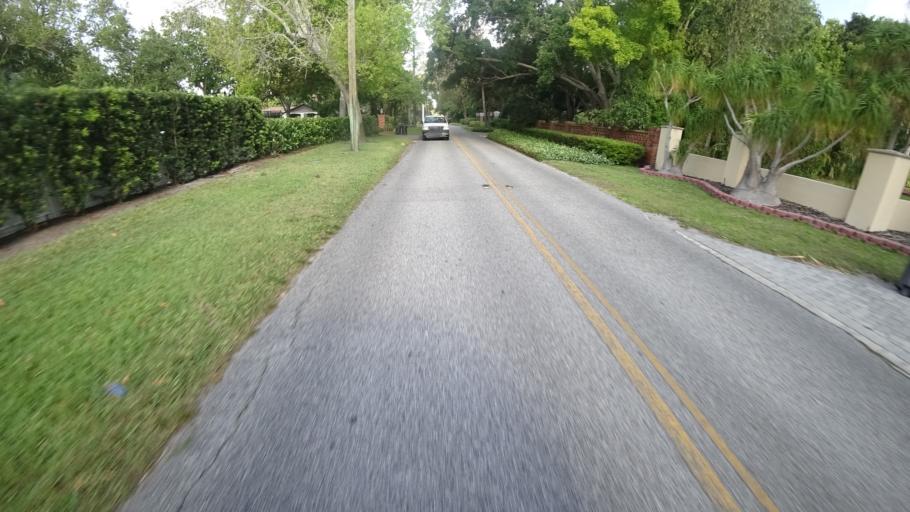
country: US
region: Florida
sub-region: Manatee County
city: West Bradenton
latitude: 27.5045
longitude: -82.6089
